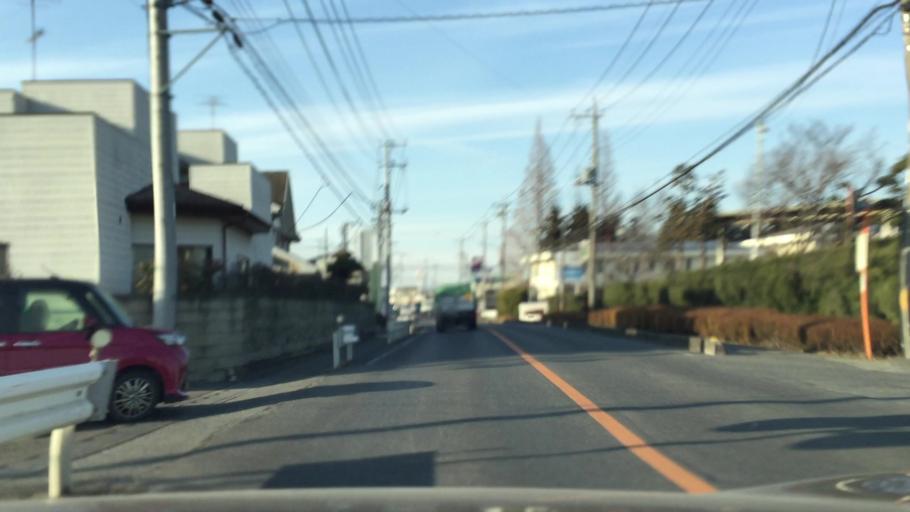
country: JP
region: Saitama
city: Menuma
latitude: 36.2126
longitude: 139.3783
